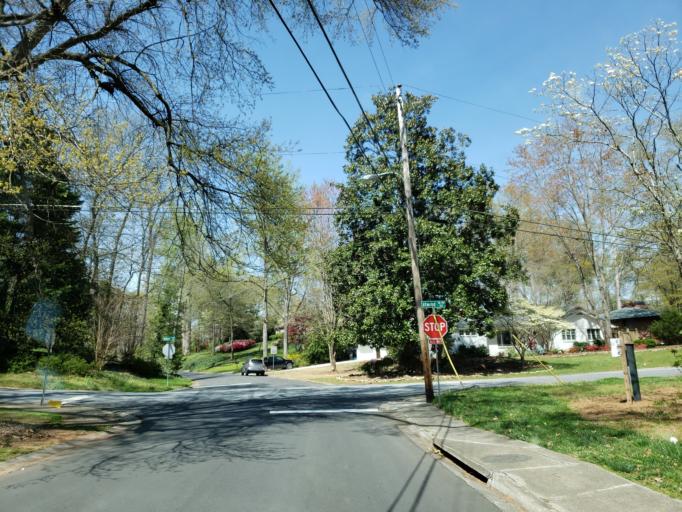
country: US
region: Georgia
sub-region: Cobb County
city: Marietta
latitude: 33.9604
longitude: -84.5588
